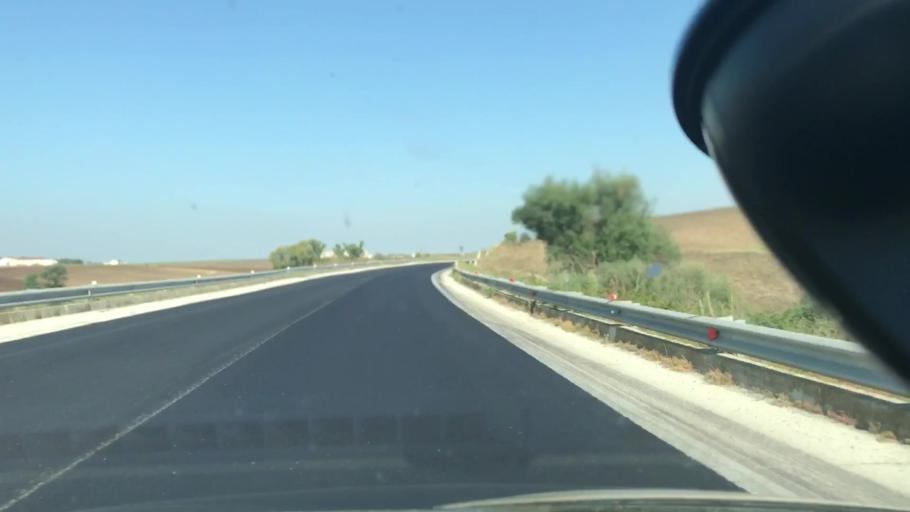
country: IT
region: Apulia
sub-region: Provincia di Barletta - Andria - Trani
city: Spinazzola
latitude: 40.9073
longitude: 16.1096
